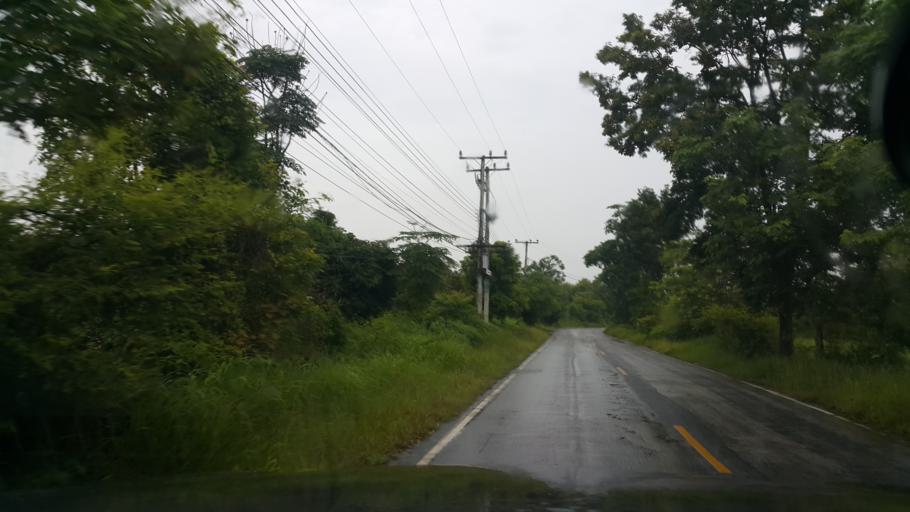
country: TH
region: Lamphun
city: Ban Thi
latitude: 18.6331
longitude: 99.1103
